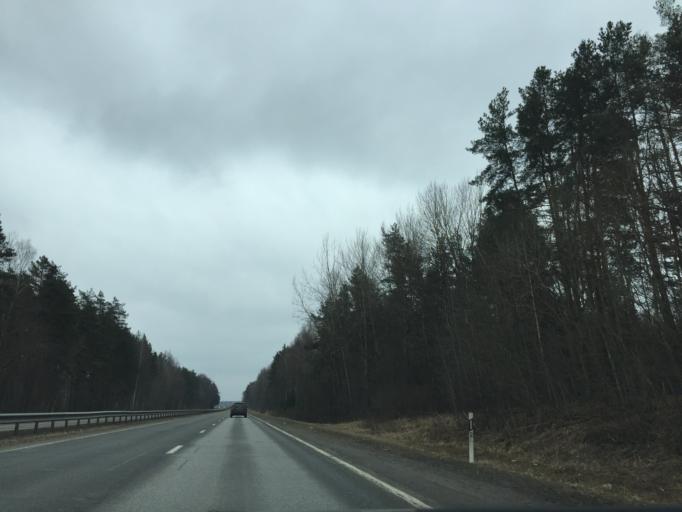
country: LV
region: Ikskile
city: Ikskile
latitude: 56.8278
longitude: 24.5213
